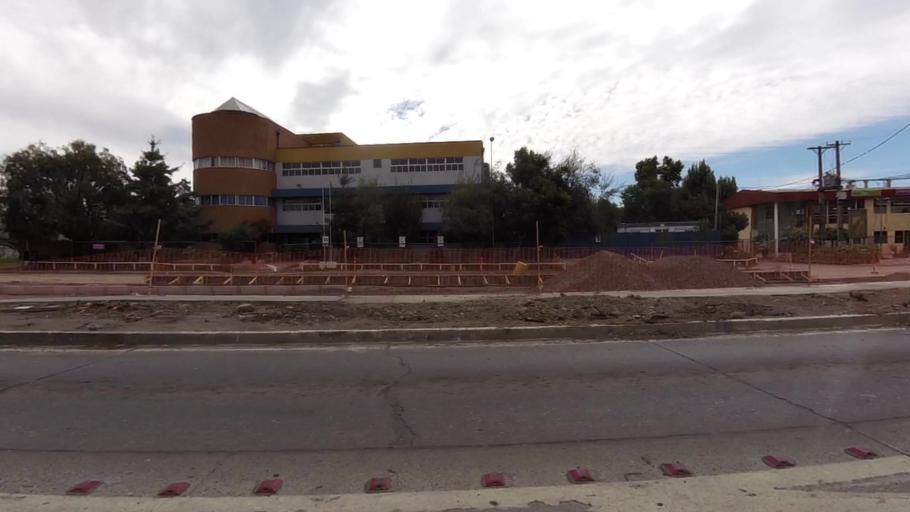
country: CL
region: O'Higgins
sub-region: Provincia de Cachapoal
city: Rancagua
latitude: -34.1441
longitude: -70.7394
